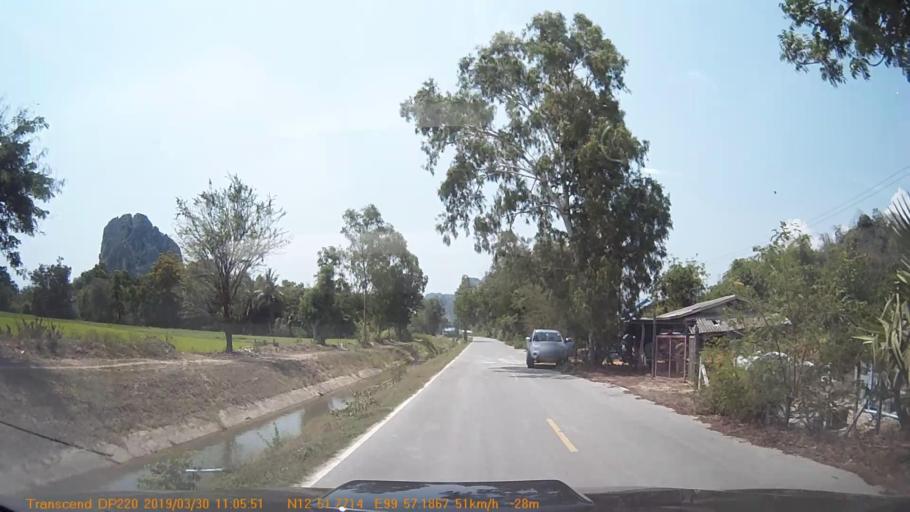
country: TH
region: Phetchaburi
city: Cha-am
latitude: 12.8626
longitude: 99.9531
